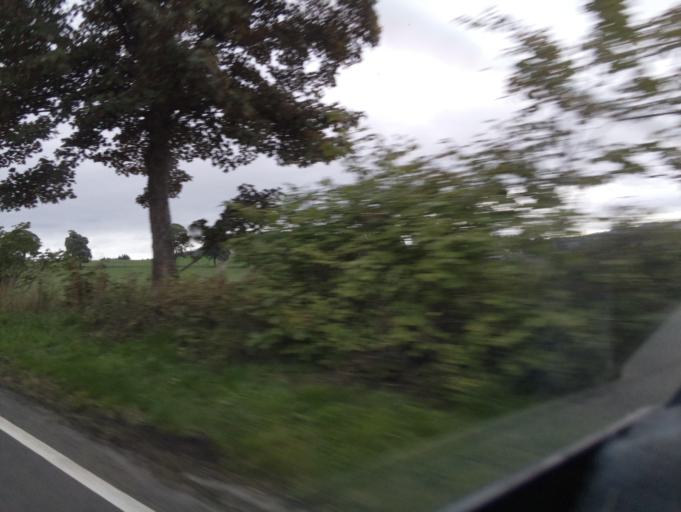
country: GB
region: Scotland
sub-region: Clackmannanshire
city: Dollar
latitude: 56.1728
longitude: -3.6367
